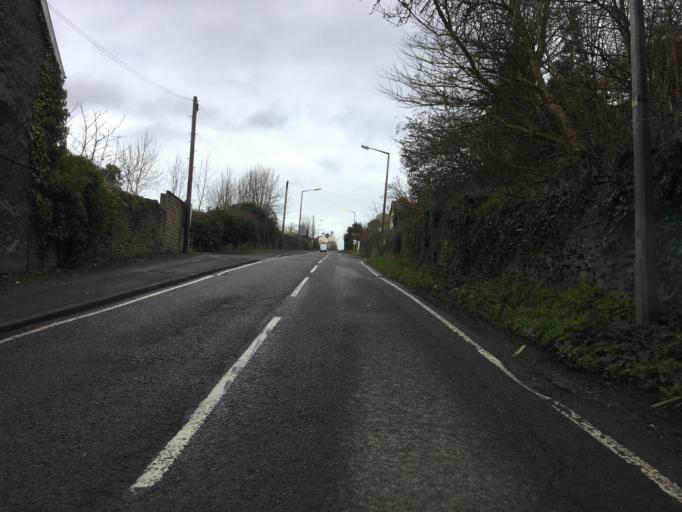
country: GB
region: England
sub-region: South Gloucestershire
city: Winterbourne
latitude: 51.5196
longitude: -2.5102
